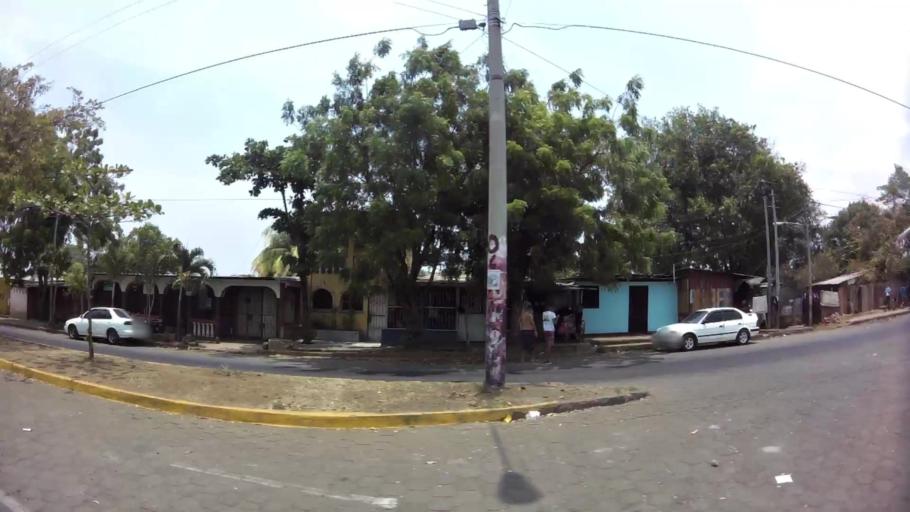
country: NI
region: Managua
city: Managua
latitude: 12.1357
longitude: -86.2884
